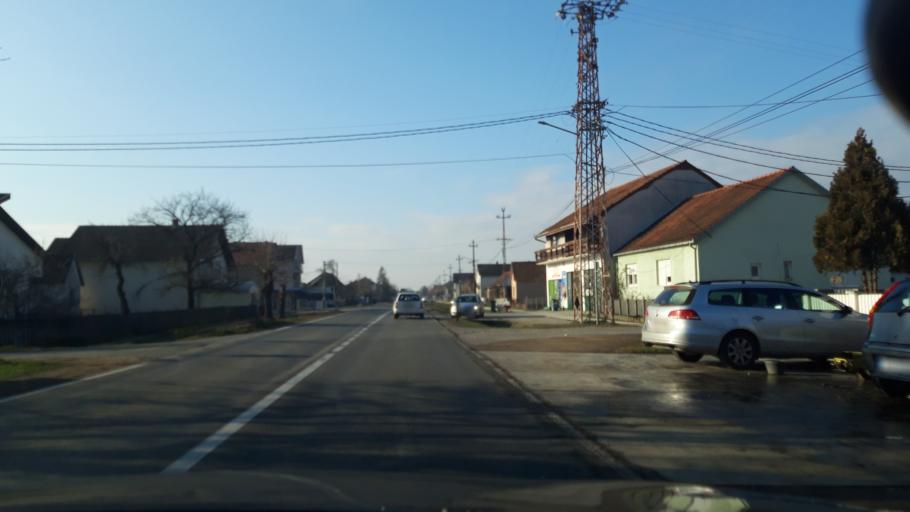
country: RS
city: Prnjavor
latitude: 44.6950
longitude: 19.3823
